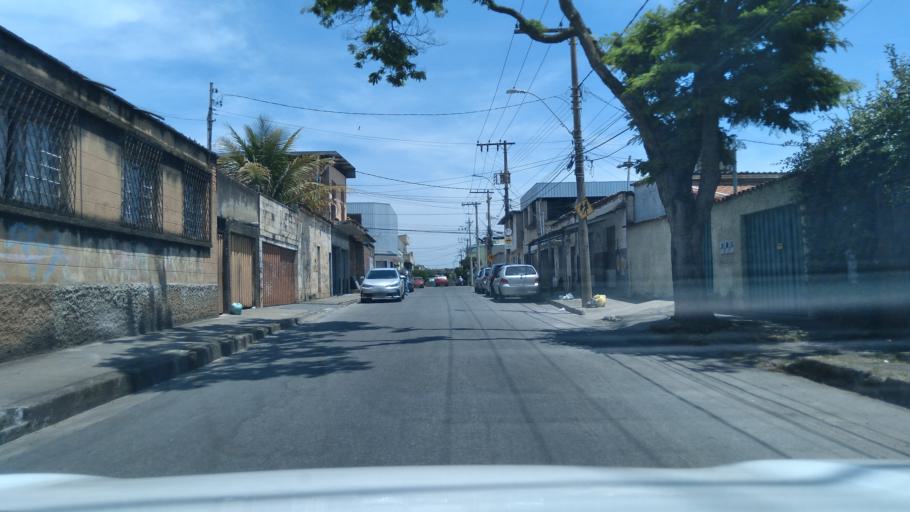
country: BR
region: Minas Gerais
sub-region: Contagem
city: Contagem
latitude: -19.8987
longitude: -44.0106
